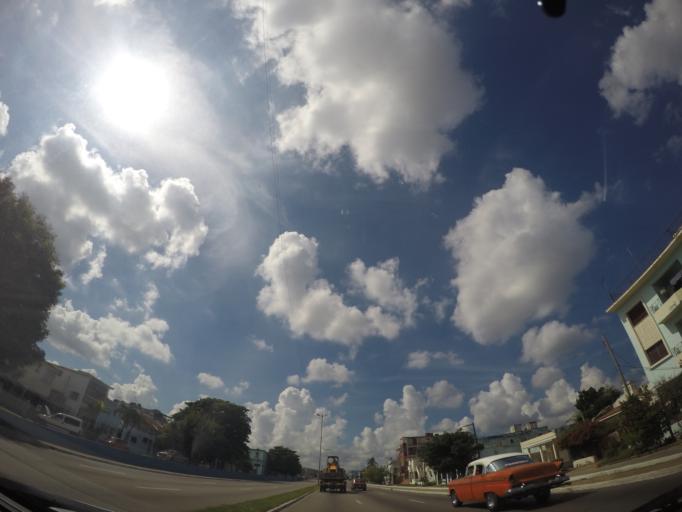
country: CU
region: La Habana
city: Cerro
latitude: 23.1093
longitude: -82.4185
